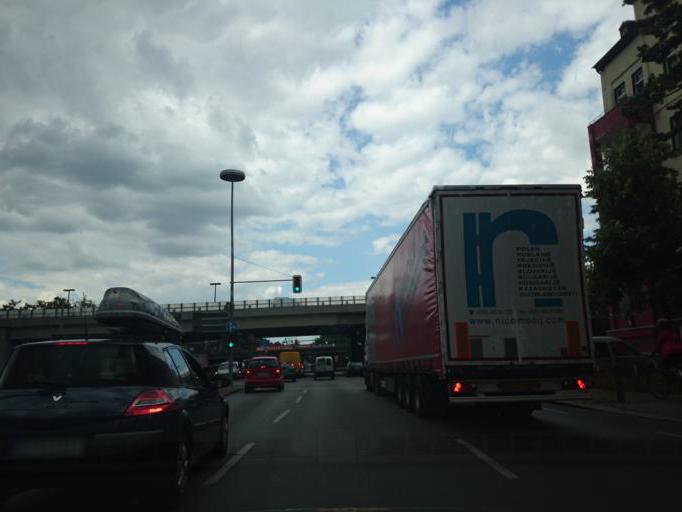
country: DE
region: Berlin
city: Tempelhof Bezirk
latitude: 52.4691
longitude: 13.3856
